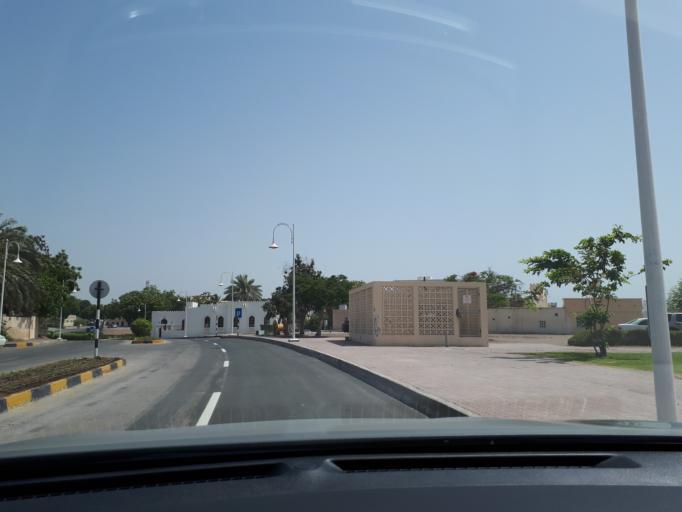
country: OM
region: Muhafazat Masqat
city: As Sib al Jadidah
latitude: 23.7112
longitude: 58.0739
